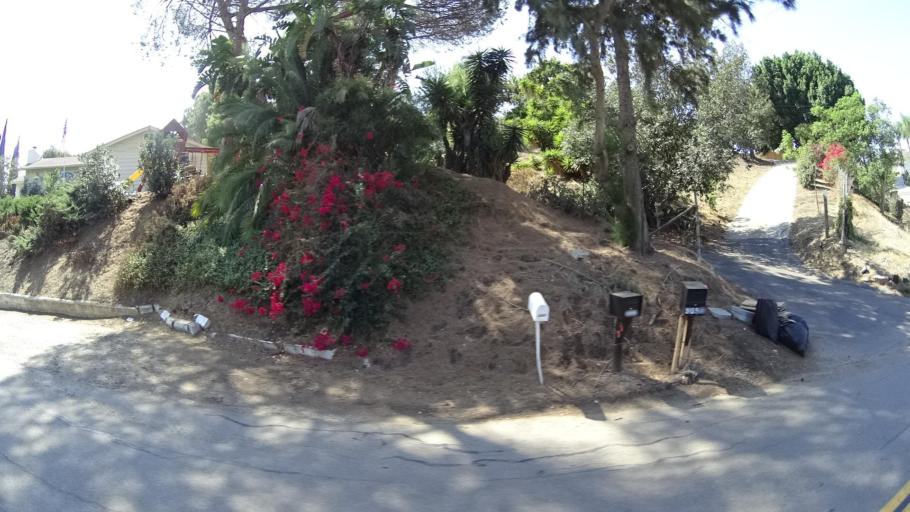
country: US
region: California
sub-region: San Diego County
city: Spring Valley
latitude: 32.7391
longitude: -116.9901
